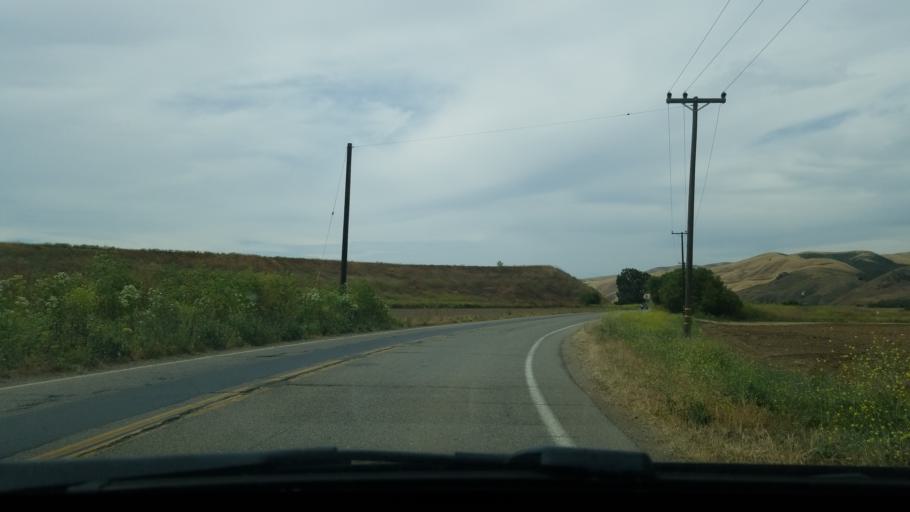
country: US
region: California
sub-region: Santa Barbara County
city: Orcutt
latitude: 34.9012
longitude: -120.3164
